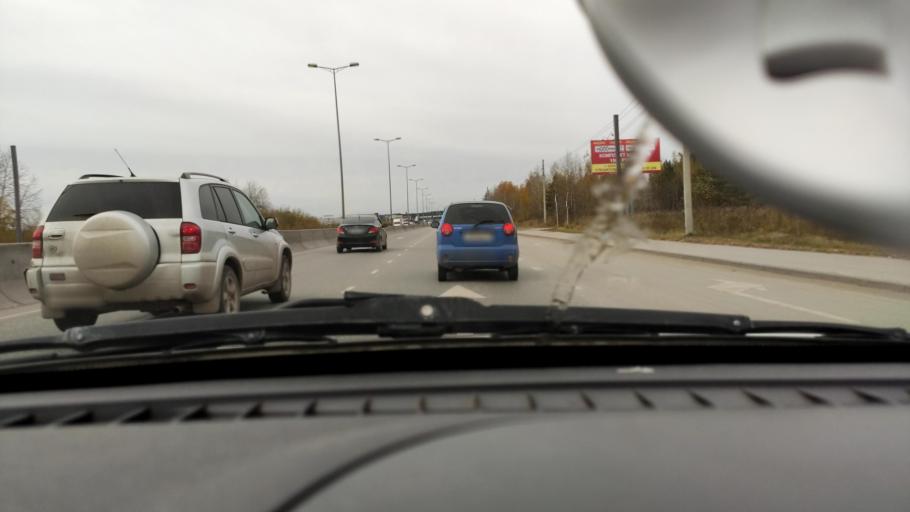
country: RU
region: Perm
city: Perm
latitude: 58.0320
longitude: 56.2104
